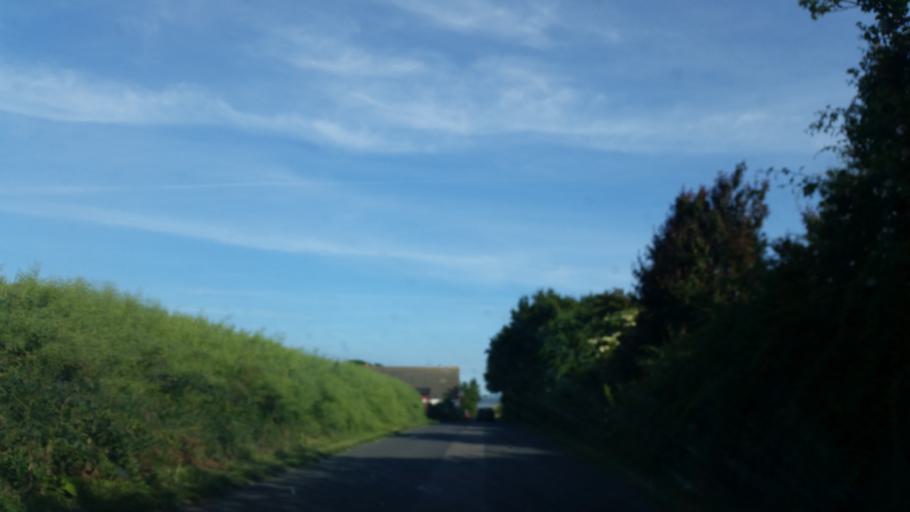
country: DK
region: Central Jutland
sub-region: Samso Kommune
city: Tranebjerg
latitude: 55.9182
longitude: 10.6340
